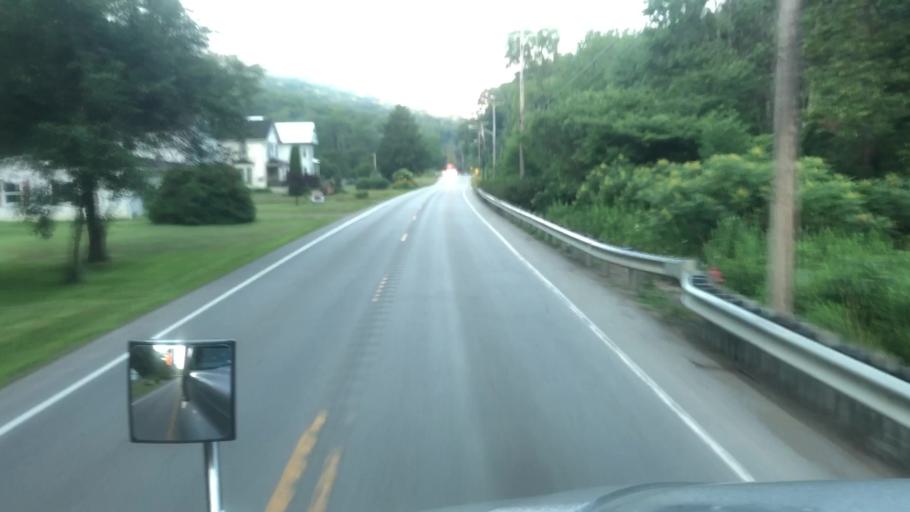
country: US
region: Pennsylvania
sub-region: Venango County
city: Hasson Heights
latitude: 41.4754
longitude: -79.6814
